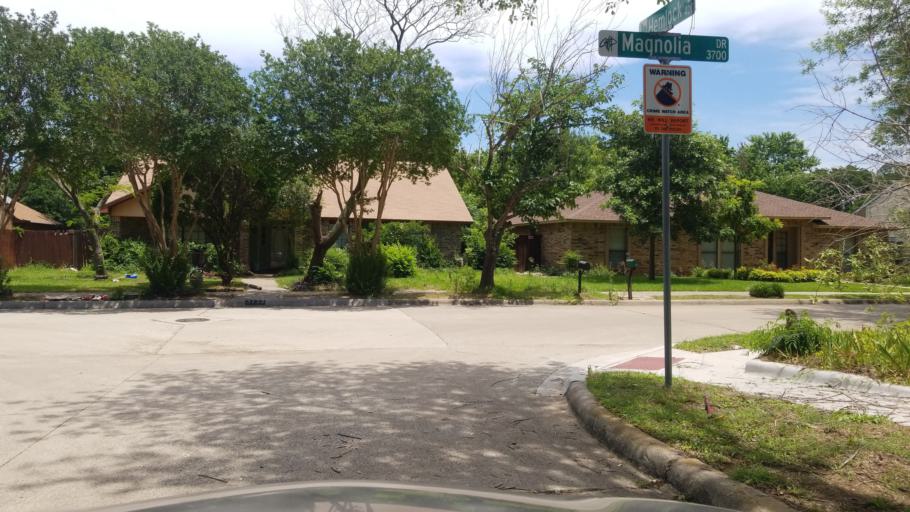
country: US
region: Texas
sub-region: Dallas County
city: Grand Prairie
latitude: 32.6826
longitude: -97.0041
